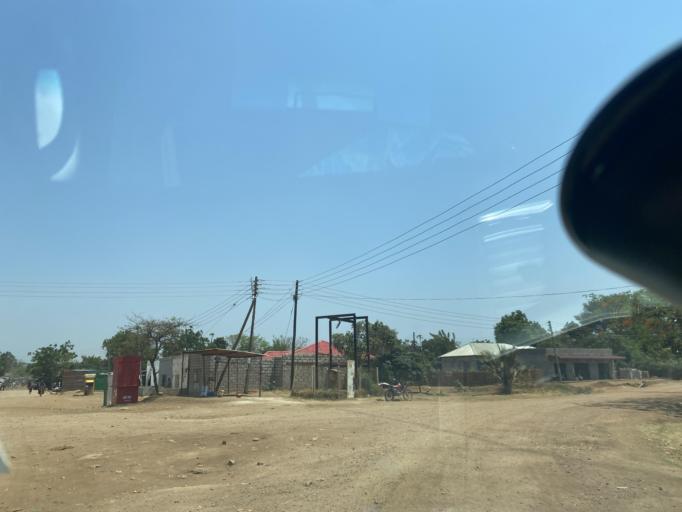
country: ZM
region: Southern
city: Nakambala
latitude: -15.5117
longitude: 27.9280
